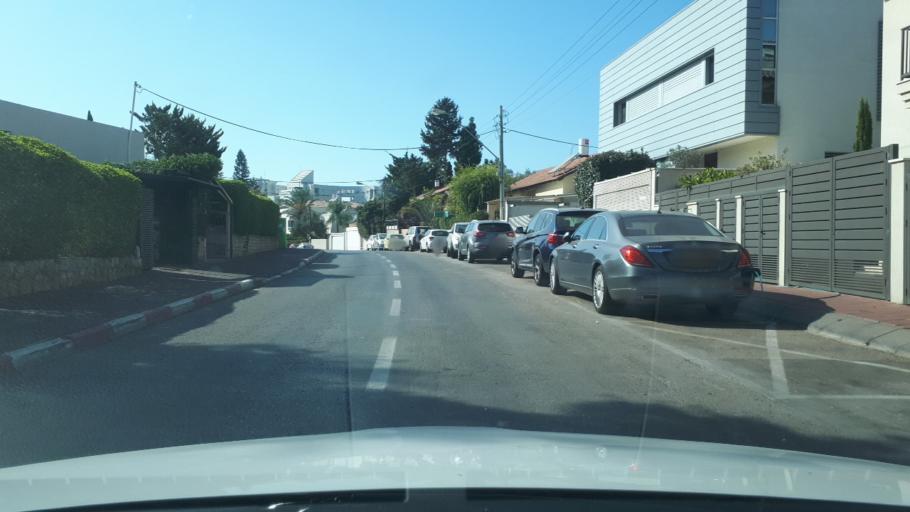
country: IL
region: Tel Aviv
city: Giv`atayim
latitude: 32.0588
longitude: 34.8242
